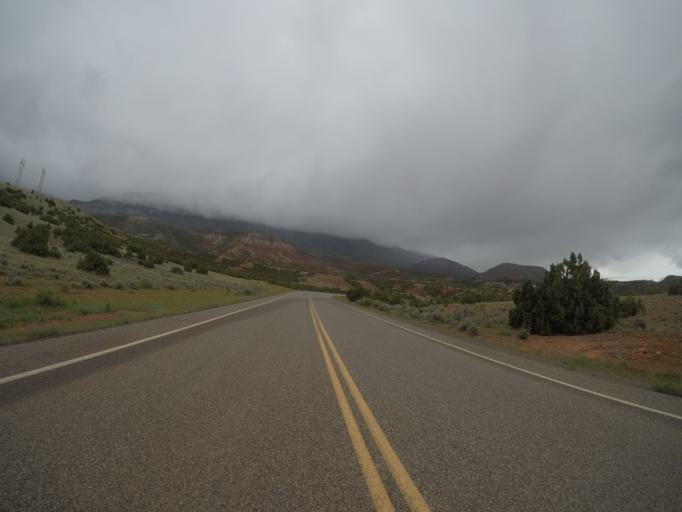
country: US
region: Wyoming
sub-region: Big Horn County
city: Lovell
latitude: 45.1058
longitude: -108.2410
